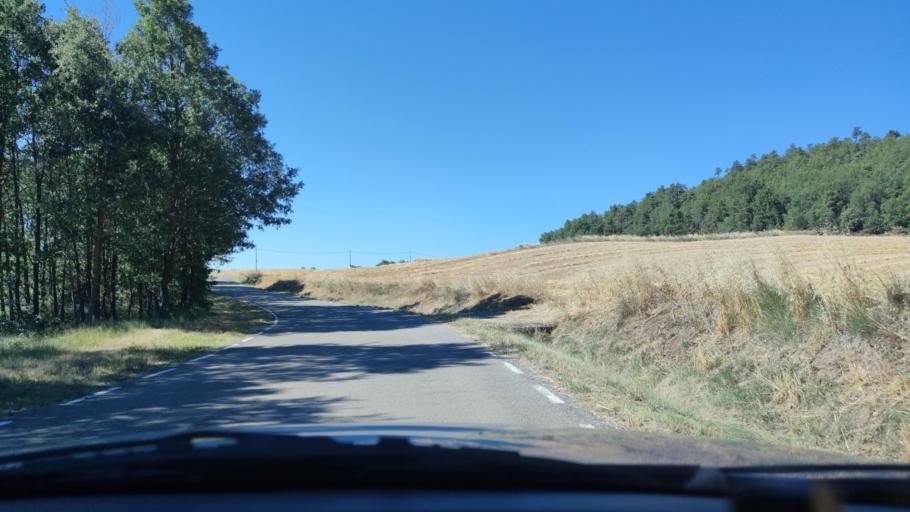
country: ES
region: Catalonia
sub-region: Provincia de Lleida
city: Solsona
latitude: 41.9681
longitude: 1.4962
